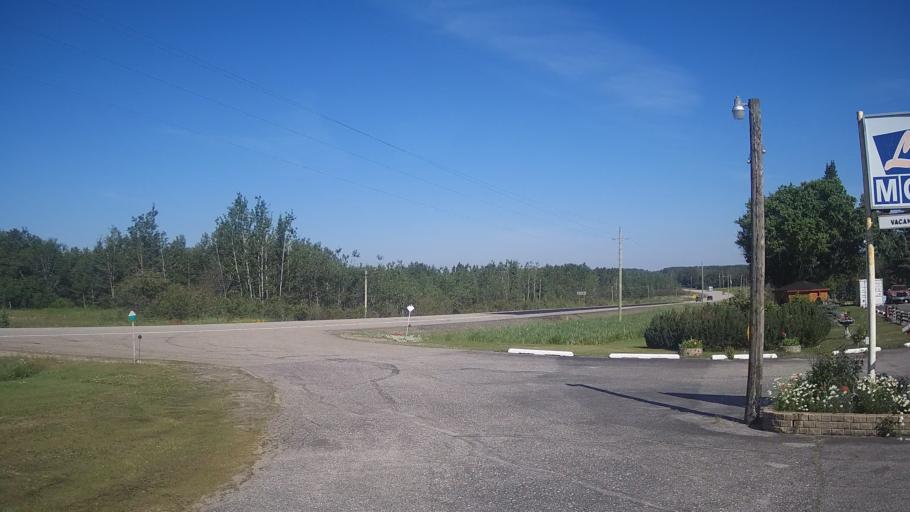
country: CA
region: Ontario
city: Dryden
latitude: 49.7360
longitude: -92.6152
